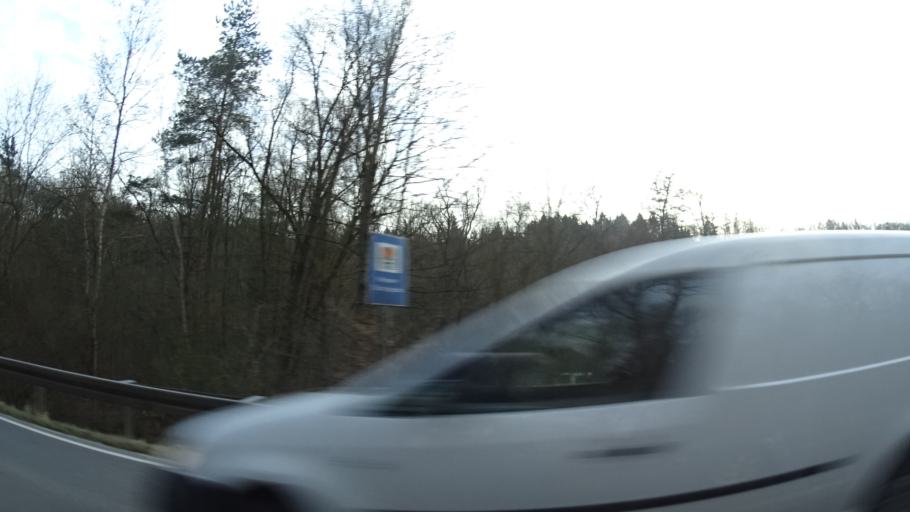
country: DE
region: Baden-Wuerttemberg
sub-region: Regierungsbezirk Stuttgart
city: Gerlingen
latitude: 48.7594
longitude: 9.0645
